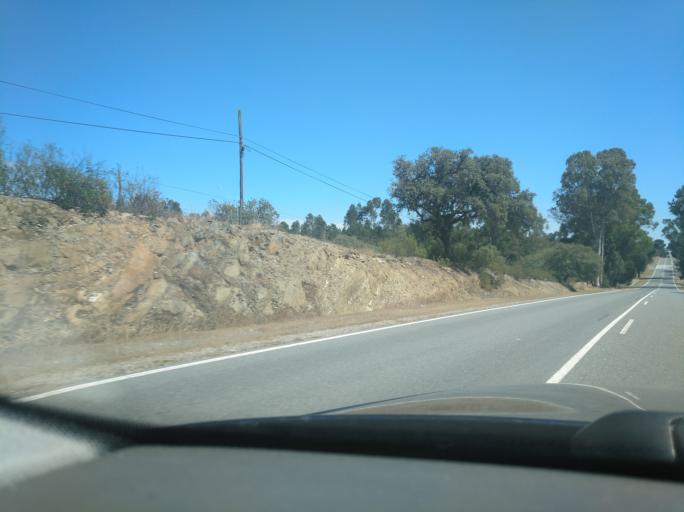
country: PT
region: Beja
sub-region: Almodovar
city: Almodovar
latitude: 37.5947
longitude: -8.0807
